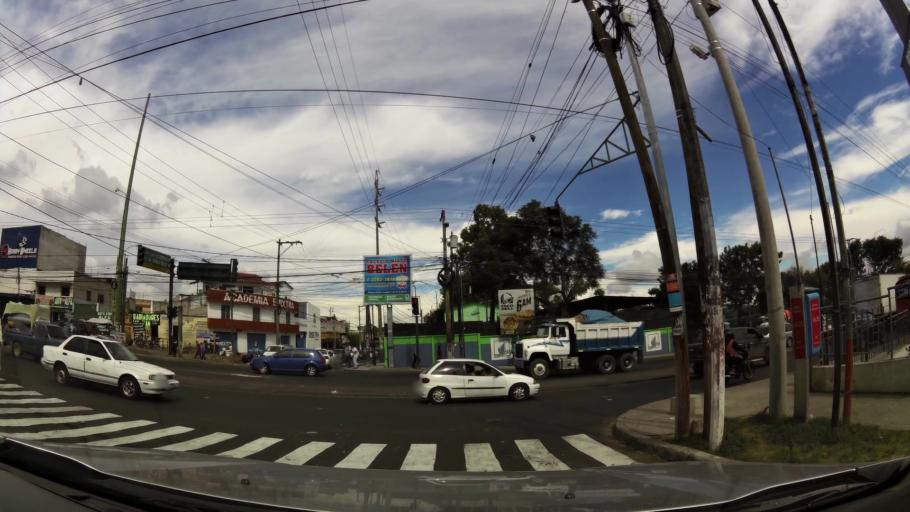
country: GT
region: Guatemala
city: Mixco
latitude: 14.6455
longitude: -90.5774
